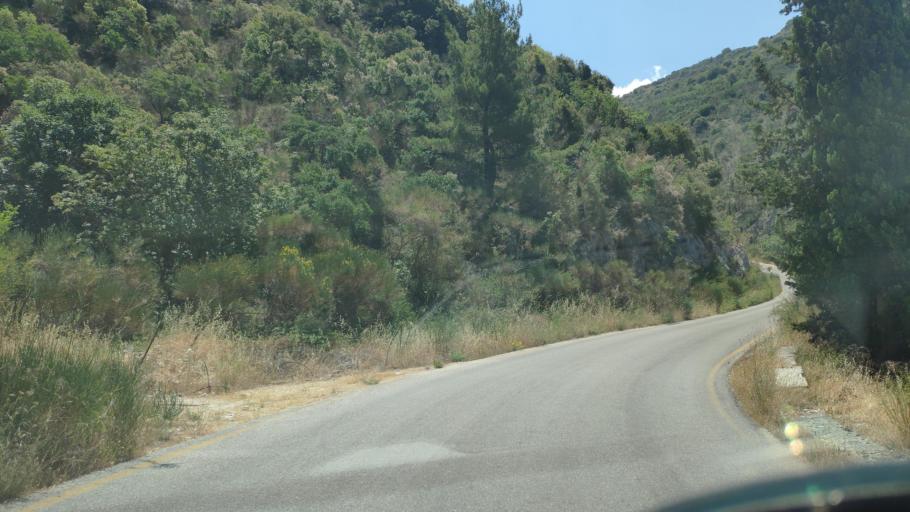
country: GR
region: Ionian Islands
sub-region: Lefkada
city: Nidri
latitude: 38.7456
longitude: 20.6216
